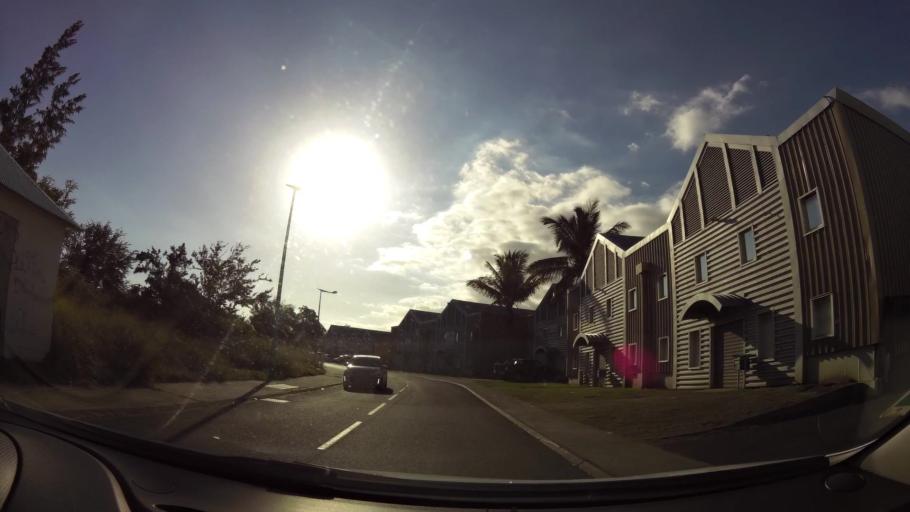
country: RE
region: Reunion
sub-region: Reunion
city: Saint-Louis
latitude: -21.2778
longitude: 55.3782
